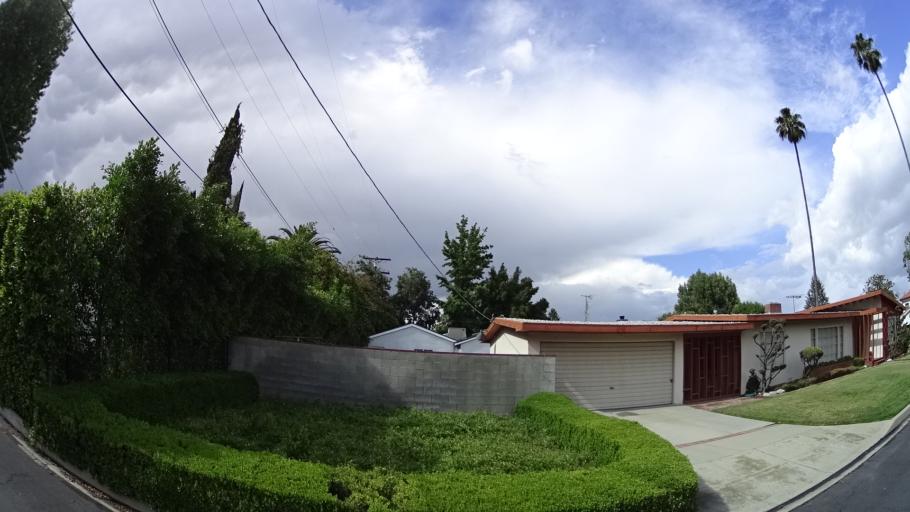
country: US
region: California
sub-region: Los Angeles County
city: Sherman Oaks
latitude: 34.1542
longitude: -118.4264
